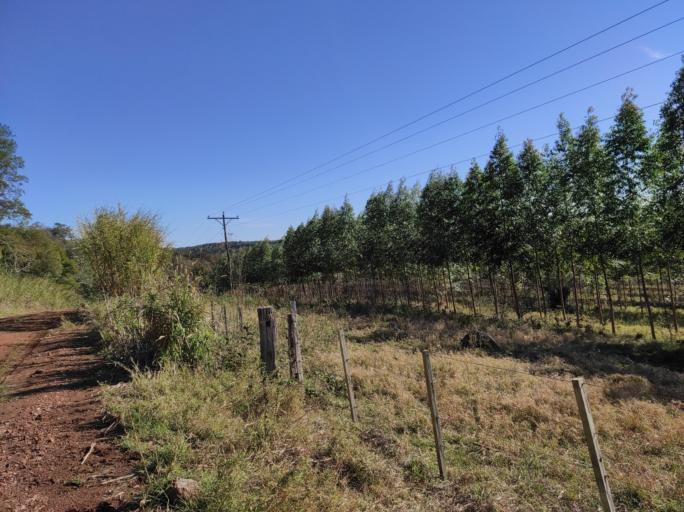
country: AR
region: Misiones
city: Capiovi
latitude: -26.9339
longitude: -54.9894
